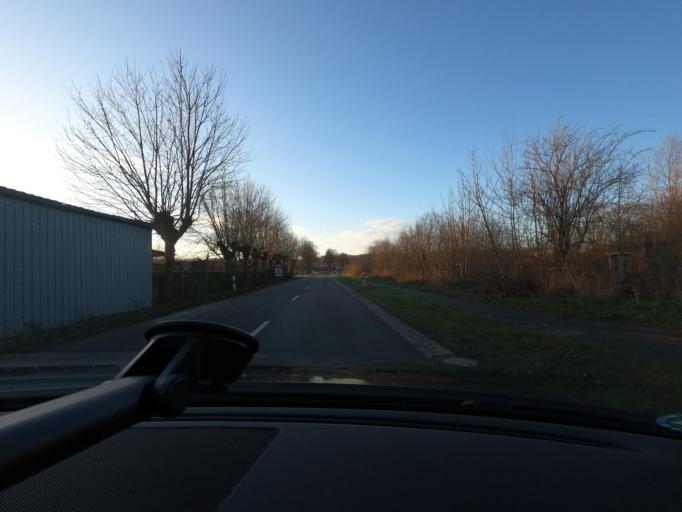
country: DE
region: Lower Saxony
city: Badenhausen
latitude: 51.7679
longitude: 10.1971
